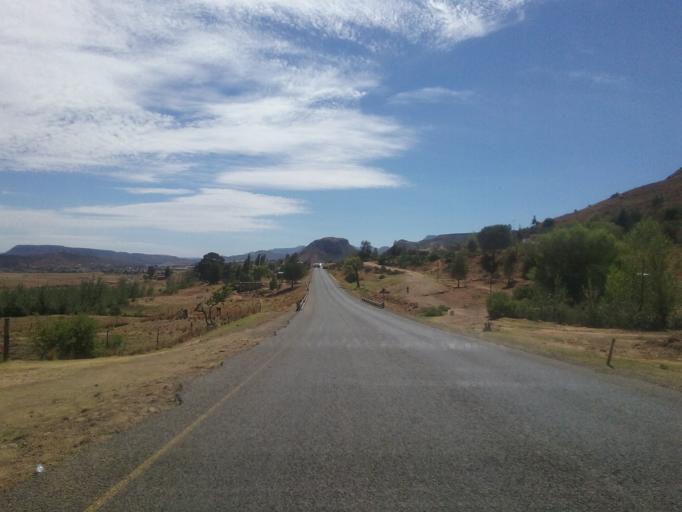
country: LS
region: Mohale's Hoek District
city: Mohale's Hoek
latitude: -30.1854
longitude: 27.4225
